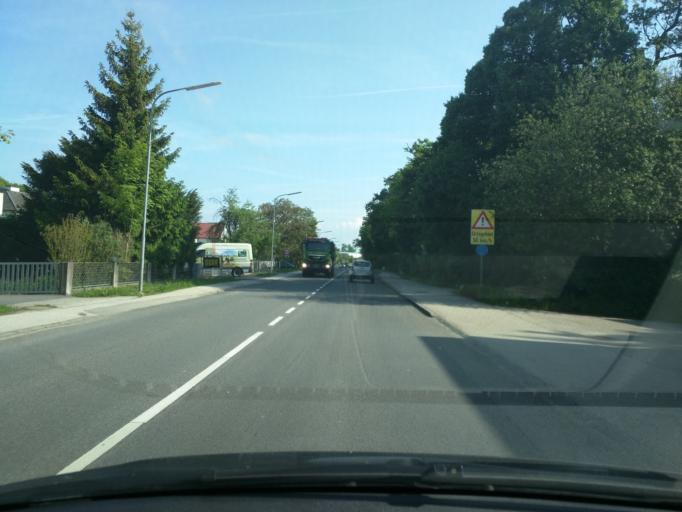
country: AT
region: Lower Austria
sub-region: Politischer Bezirk Amstetten
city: Kematen an der Ybbs
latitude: 48.0299
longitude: 14.7723
